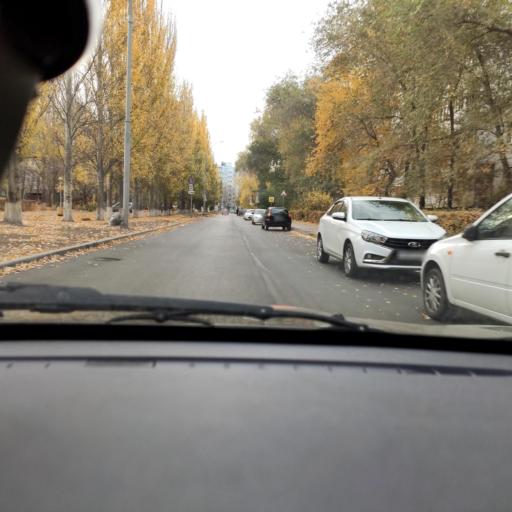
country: RU
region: Samara
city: Tol'yatti
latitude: 53.5236
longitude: 49.3018
